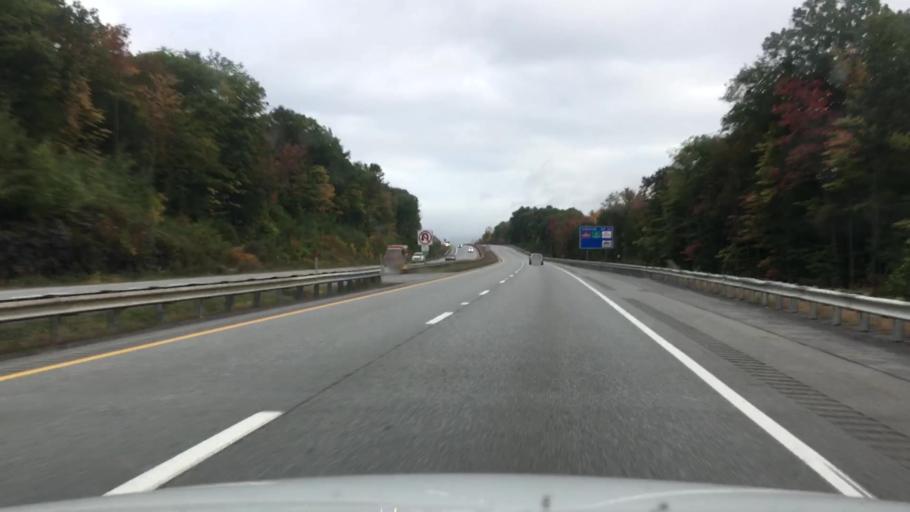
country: US
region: Maine
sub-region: Cumberland County
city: Cumberland Center
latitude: 43.8555
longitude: -70.3230
